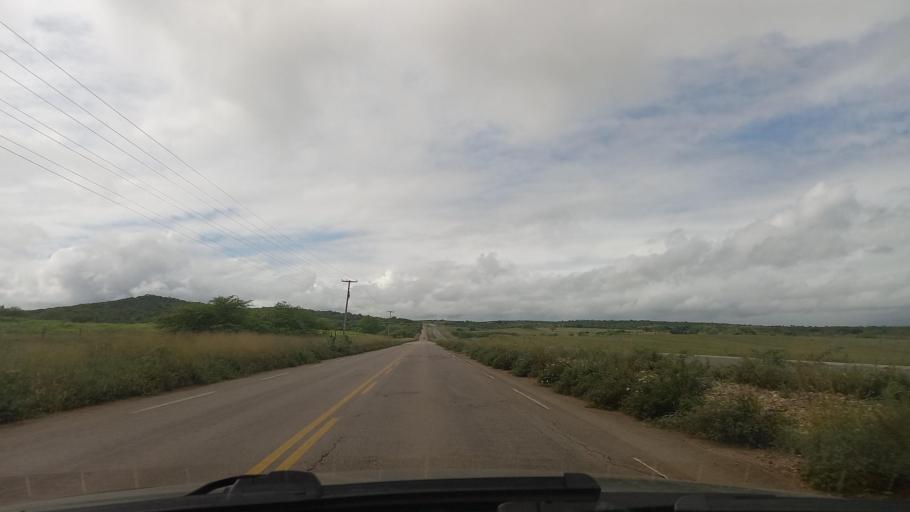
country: BR
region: Alagoas
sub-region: Batalha
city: Batalha
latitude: -9.6545
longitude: -37.1791
